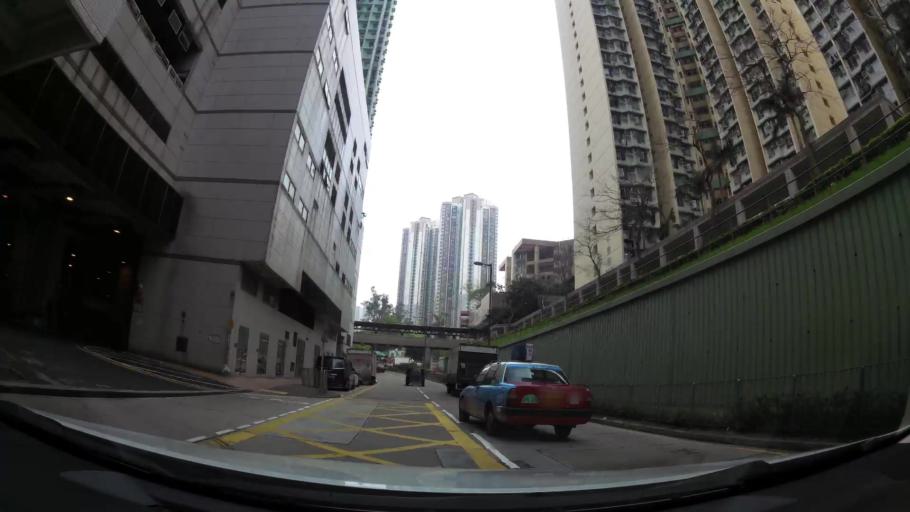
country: HK
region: Kowloon City
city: Kowloon
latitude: 22.3073
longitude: 114.2358
